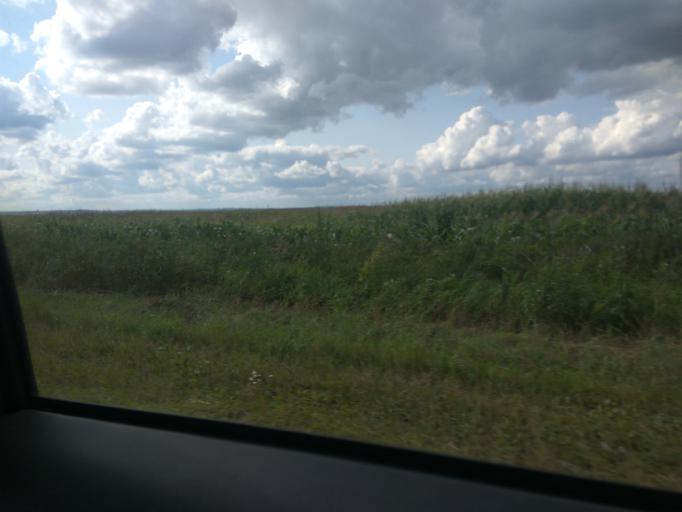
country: RU
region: Moskovskaya
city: Ramenskoye
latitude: 55.5158
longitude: 38.2676
